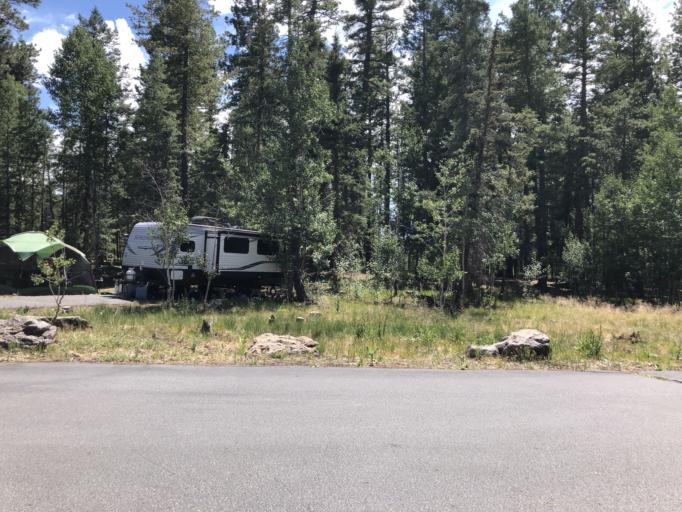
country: US
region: Arizona
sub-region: Apache County
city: Eagar
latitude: 33.8777
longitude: -109.4021
